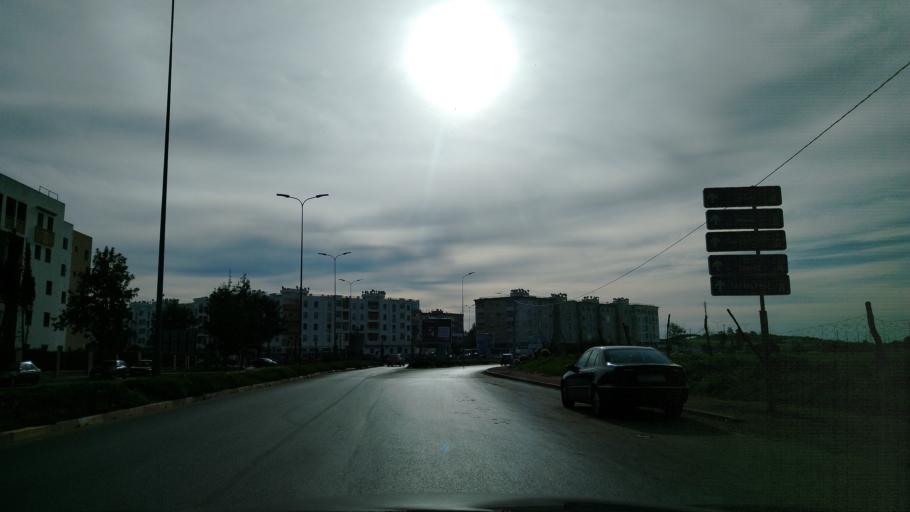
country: MA
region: Rabat-Sale-Zemmour-Zaer
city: Sale
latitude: 33.9894
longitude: -6.7401
